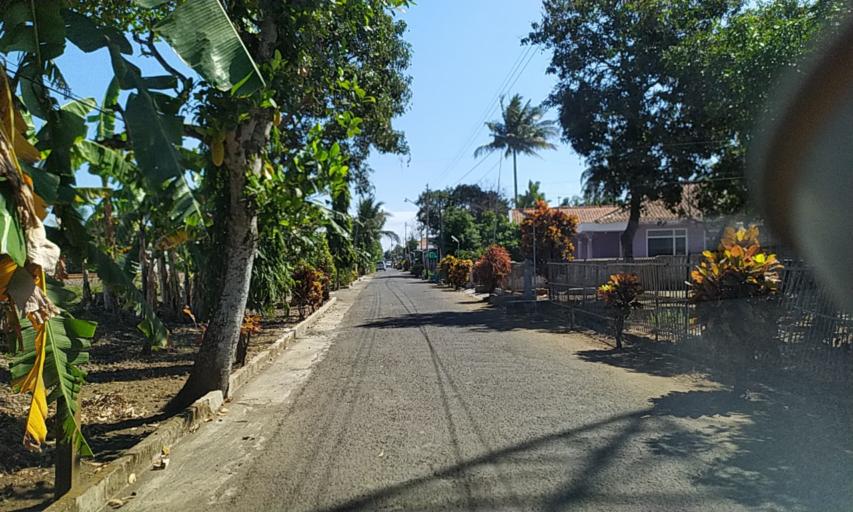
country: ID
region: Central Java
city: Rejanegara
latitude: -7.6863
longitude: 109.0405
